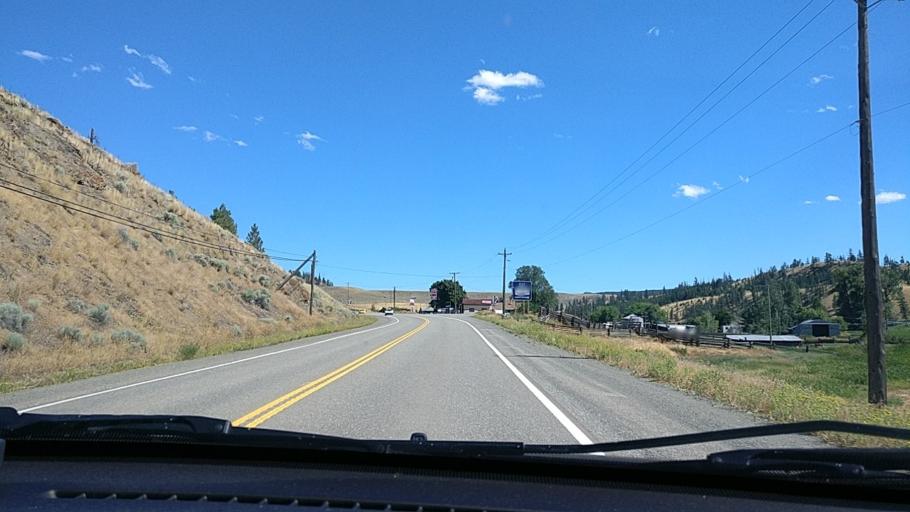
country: CA
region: British Columbia
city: Kamloops
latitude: 50.6643
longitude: -120.5573
